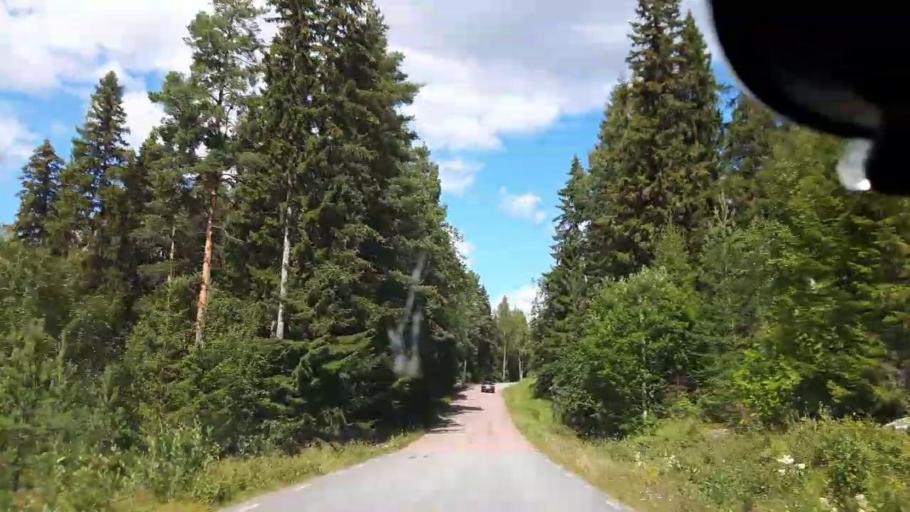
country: SE
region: Jaemtland
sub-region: Ragunda Kommun
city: Hammarstrand
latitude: 62.9381
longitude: 16.6919
